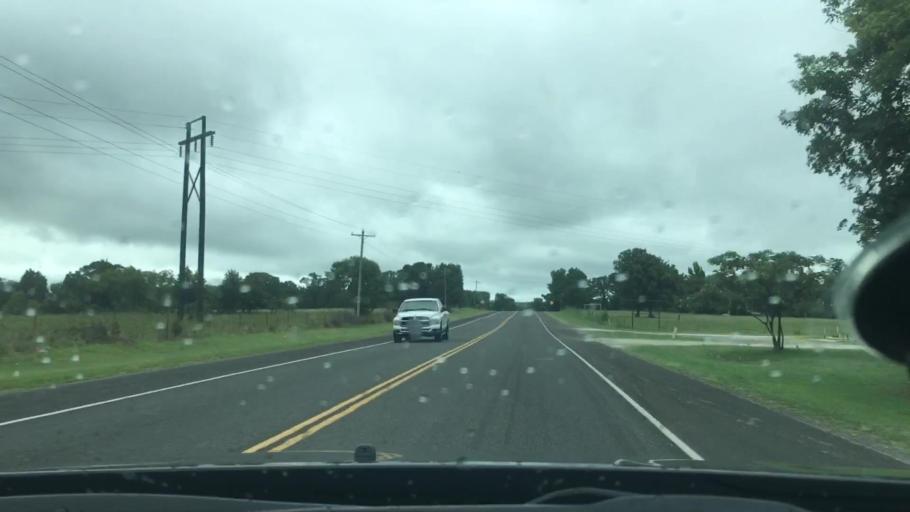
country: US
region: Oklahoma
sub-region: Sequoyah County
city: Vian
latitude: 35.5700
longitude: -94.9852
